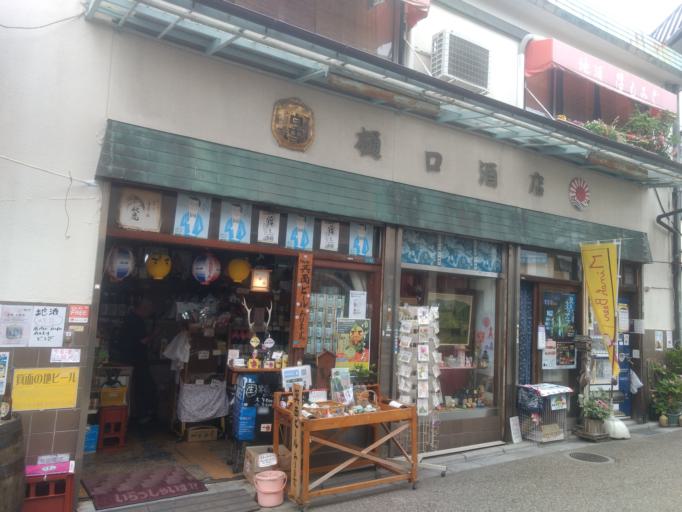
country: JP
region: Osaka
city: Mino
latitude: 34.8360
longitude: 135.4684
